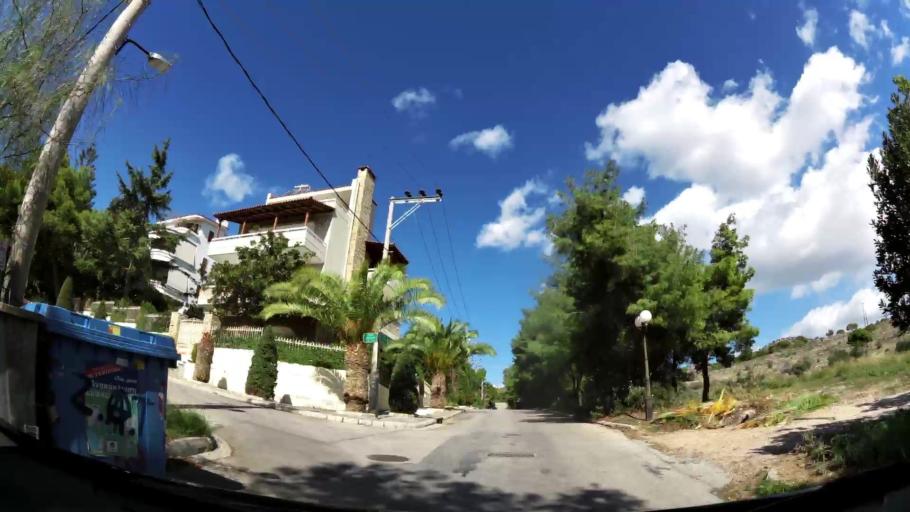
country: GR
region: Attica
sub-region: Nomarchia Anatolikis Attikis
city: Voula
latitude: 37.8406
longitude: 23.7844
